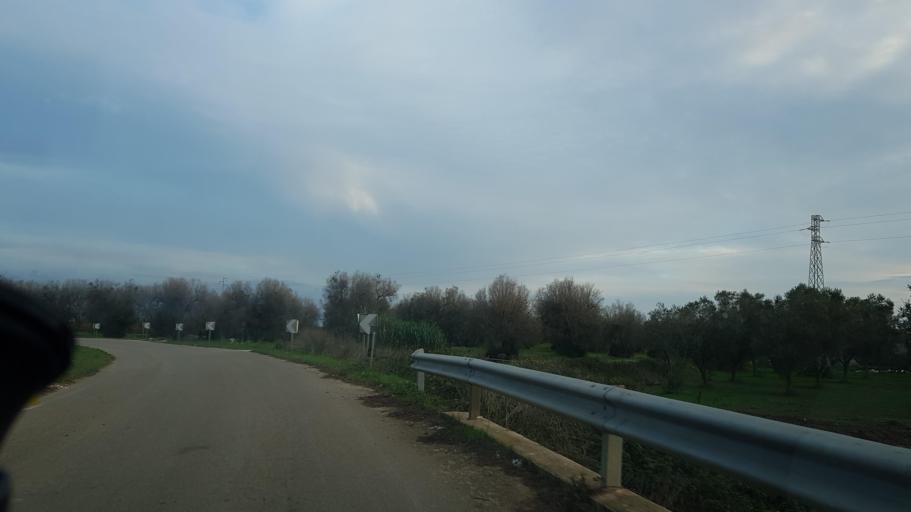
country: IT
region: Apulia
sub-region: Provincia di Brindisi
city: Latiano
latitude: 40.5393
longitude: 17.7415
